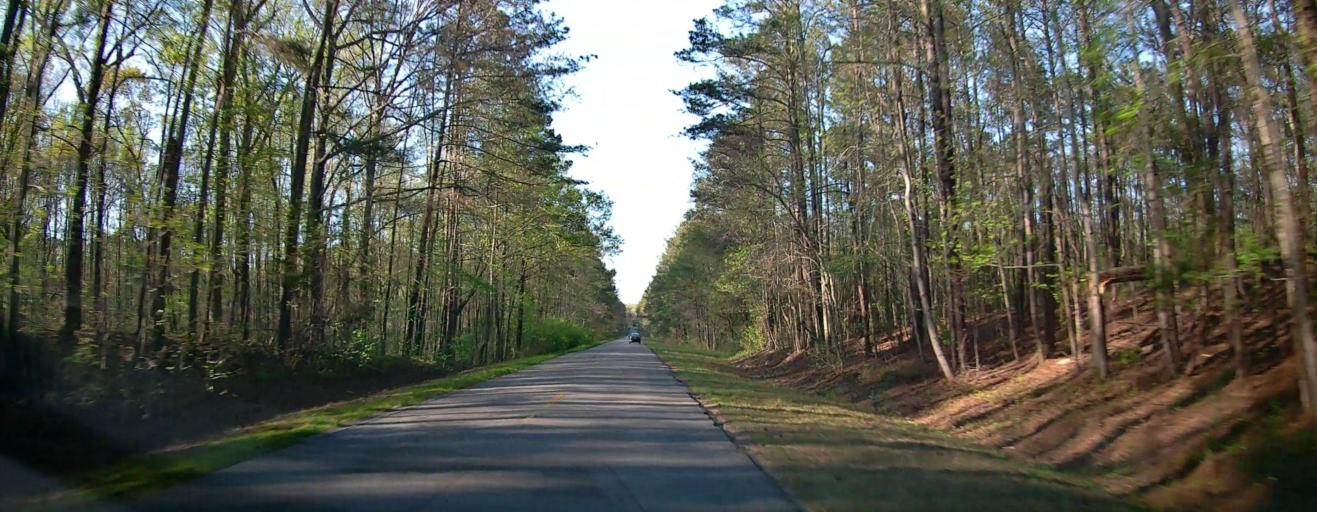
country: US
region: Georgia
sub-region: Butts County
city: Indian Springs
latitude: 33.2979
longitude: -83.8966
